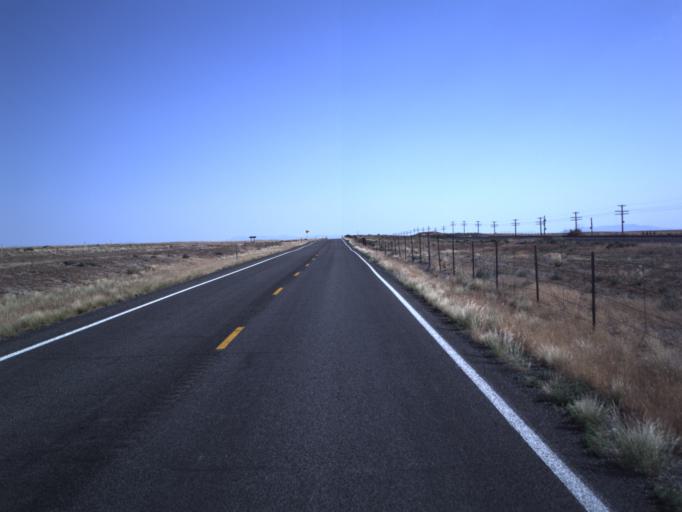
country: US
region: Utah
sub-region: Millard County
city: Delta
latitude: 38.9802
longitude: -112.7954
